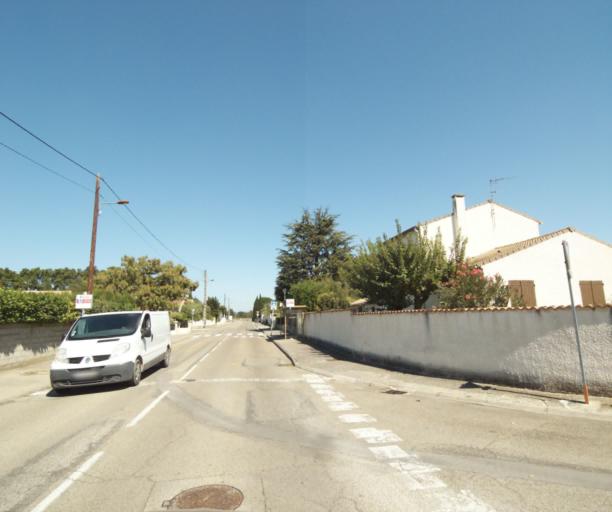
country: FR
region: Languedoc-Roussillon
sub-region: Departement du Gard
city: Rodilhan
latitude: 43.8308
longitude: 4.4317
